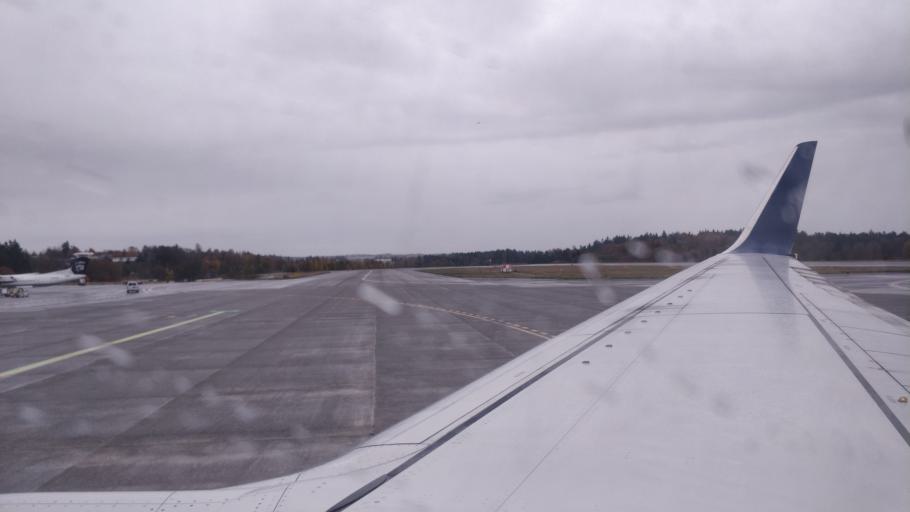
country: US
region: Washington
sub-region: King County
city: SeaTac
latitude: 47.4373
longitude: -122.3048
